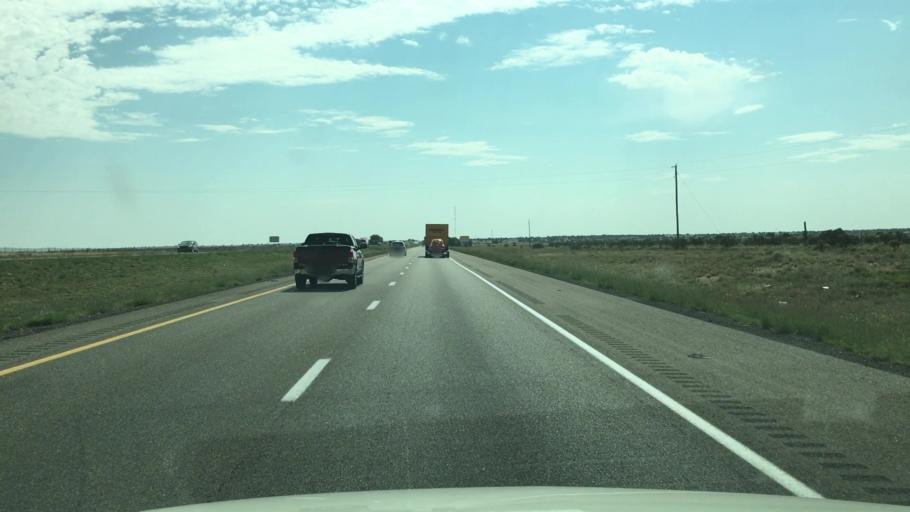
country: US
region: New Mexico
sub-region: Guadalupe County
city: Santa Rosa
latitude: 34.9739
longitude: -104.9454
